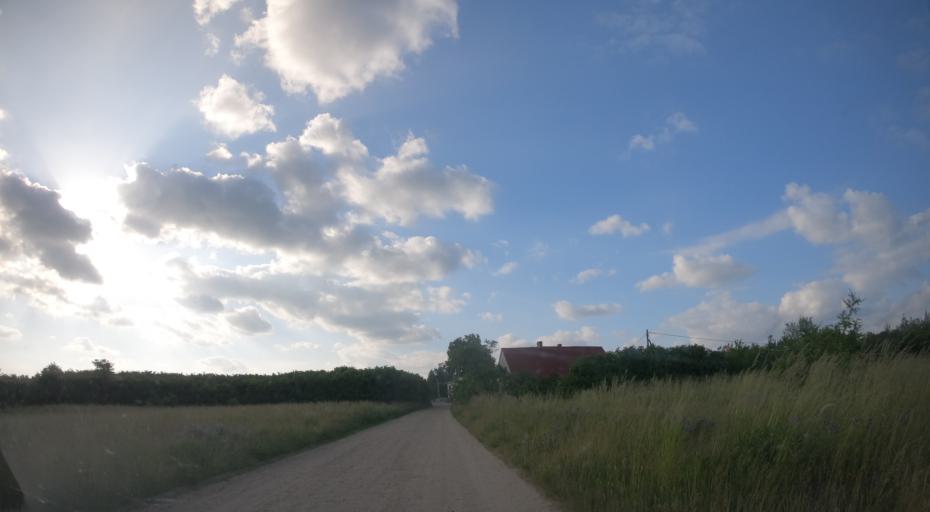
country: PL
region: Lubusz
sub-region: Powiat gorzowski
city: Santok
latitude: 52.7423
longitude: 15.3963
